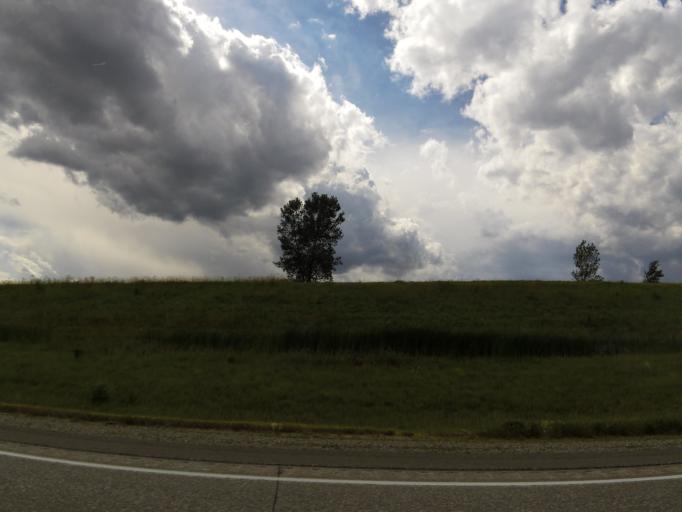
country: US
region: Iowa
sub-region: Washington County
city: Washington
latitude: 41.2758
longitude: -91.5369
